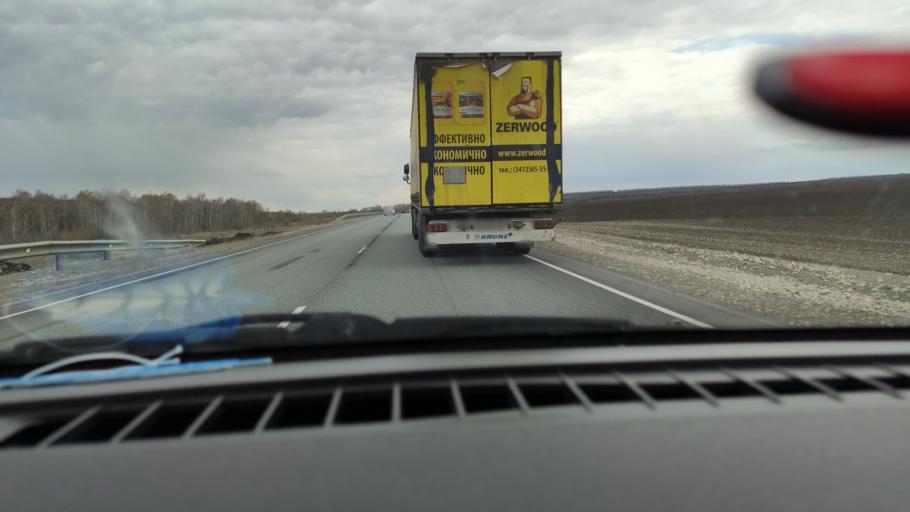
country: RU
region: Saratov
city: Yelshanka
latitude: 51.8571
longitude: 46.4951
